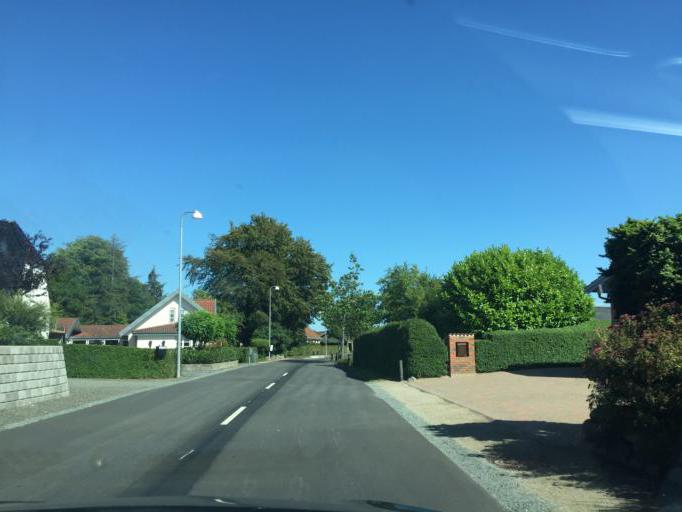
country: DK
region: South Denmark
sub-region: Nordfyns Kommune
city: Sonderso
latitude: 55.4857
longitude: 10.2567
